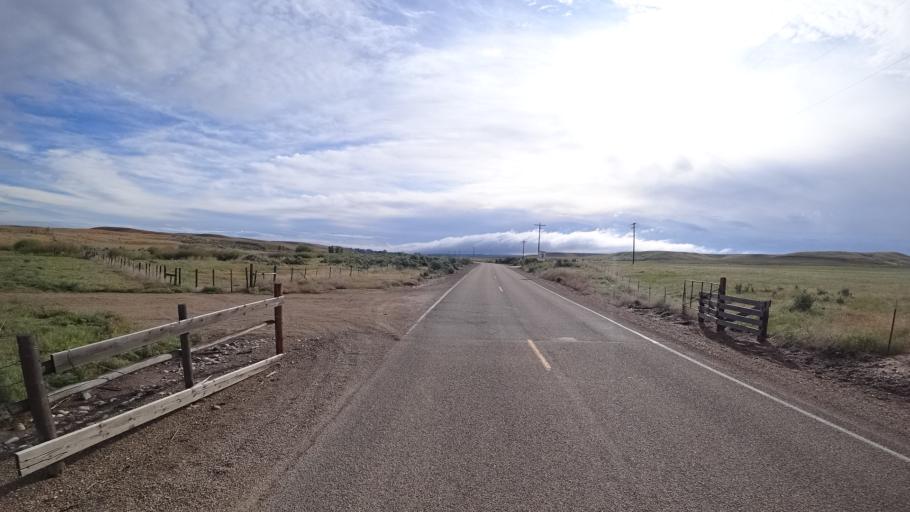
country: US
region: Idaho
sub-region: Ada County
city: Star
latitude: 43.7589
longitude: -116.5127
